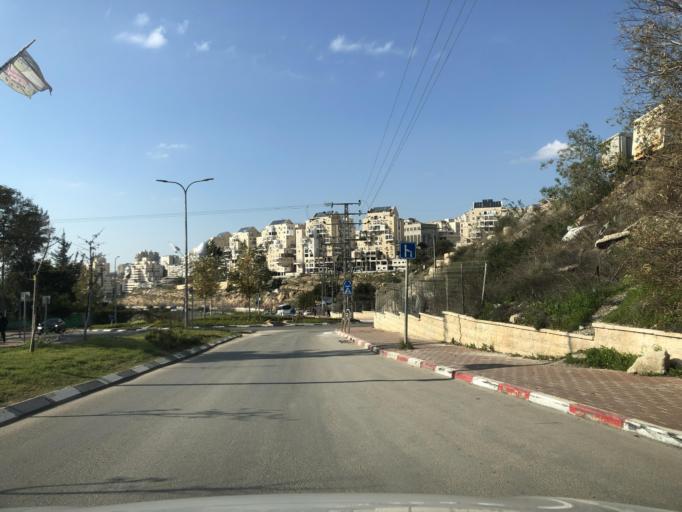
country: IL
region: Jerusalem
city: Modiin Ilit
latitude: 31.9348
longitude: 35.0479
